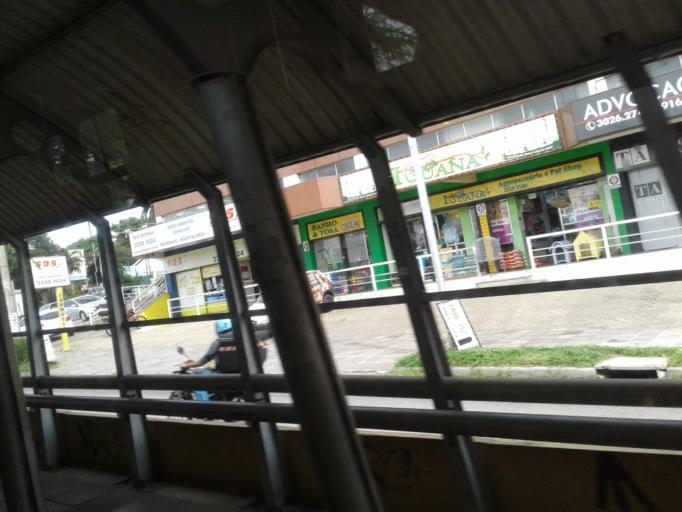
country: BR
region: Rio Grande do Sul
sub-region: Porto Alegre
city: Porto Alegre
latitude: -30.0723
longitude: -51.1934
